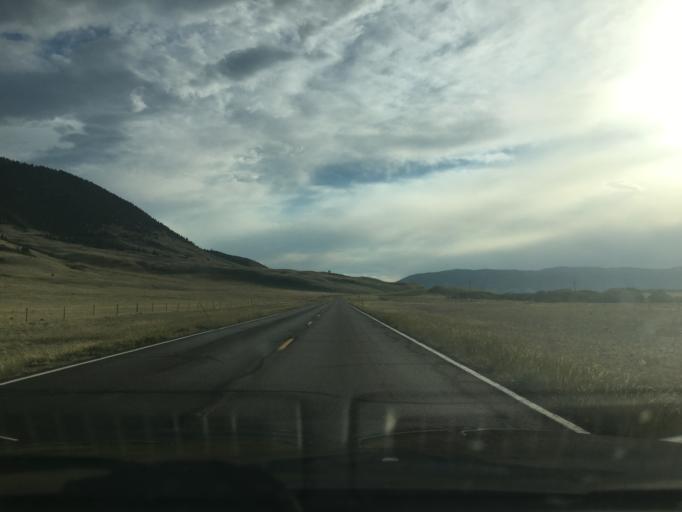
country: US
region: Wyoming
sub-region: Albany County
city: Laramie
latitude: 41.2887
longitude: -106.0357
